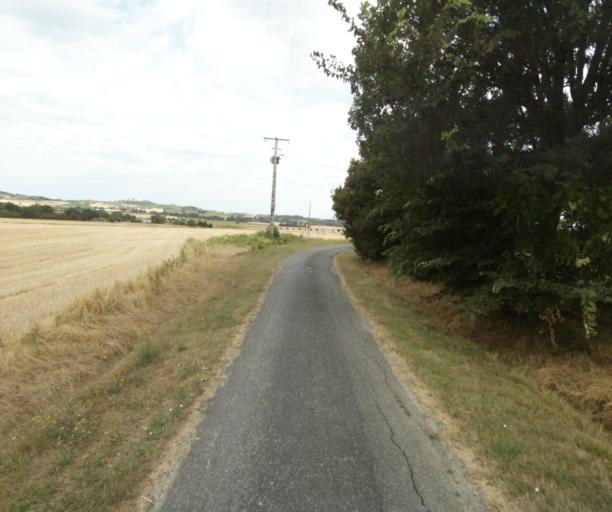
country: FR
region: Midi-Pyrenees
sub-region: Departement de la Haute-Garonne
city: Saint-Felix-Lauragais
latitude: 43.4318
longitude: 1.9258
